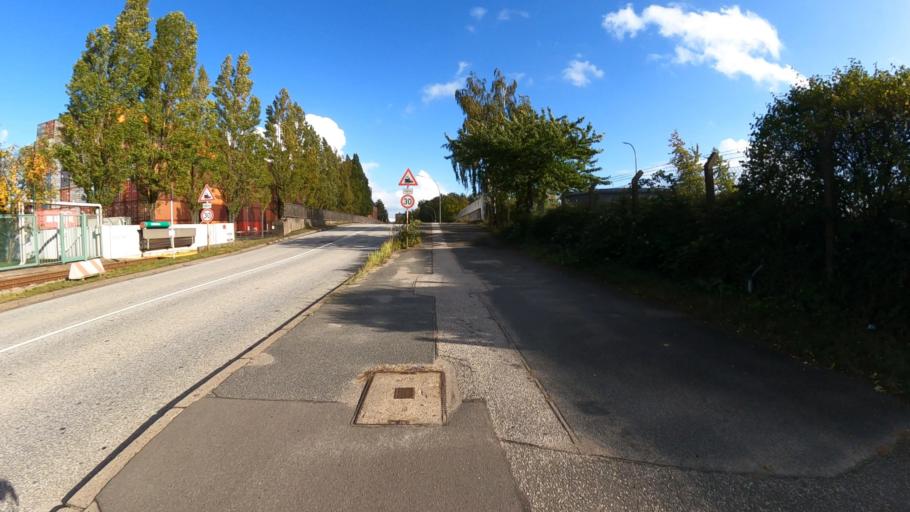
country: DE
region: Hamburg
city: Kleiner Grasbrook
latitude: 53.5129
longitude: 9.9626
